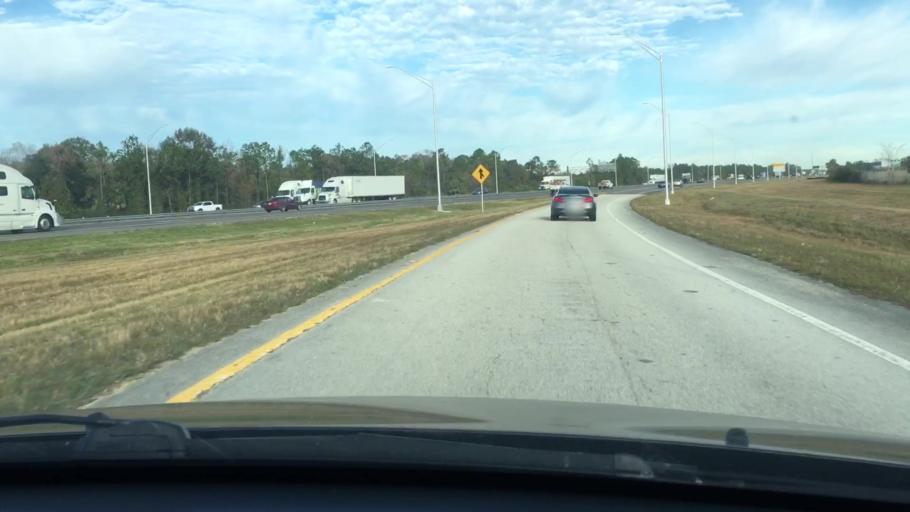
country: US
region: Florida
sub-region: Volusia County
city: Holly Hill
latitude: 29.2241
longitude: -81.1040
